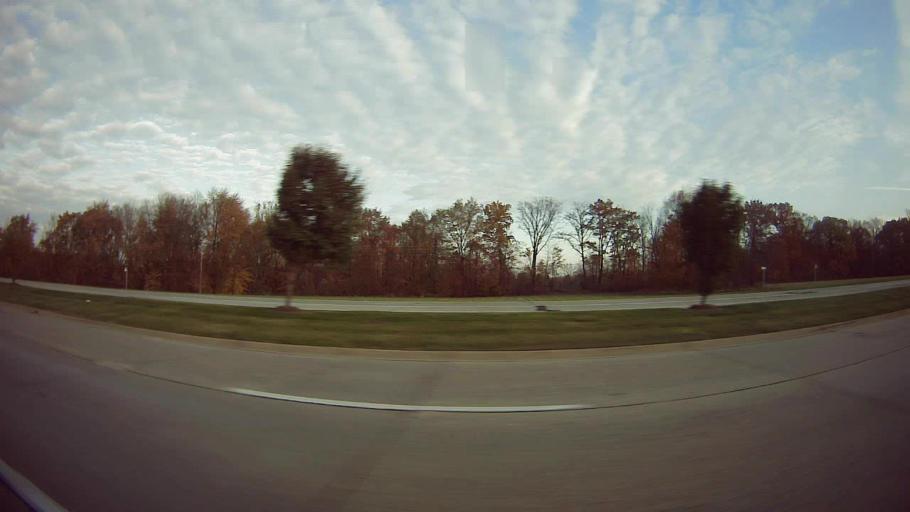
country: US
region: Michigan
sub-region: Macomb County
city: Fraser
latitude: 42.5668
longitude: -82.9802
